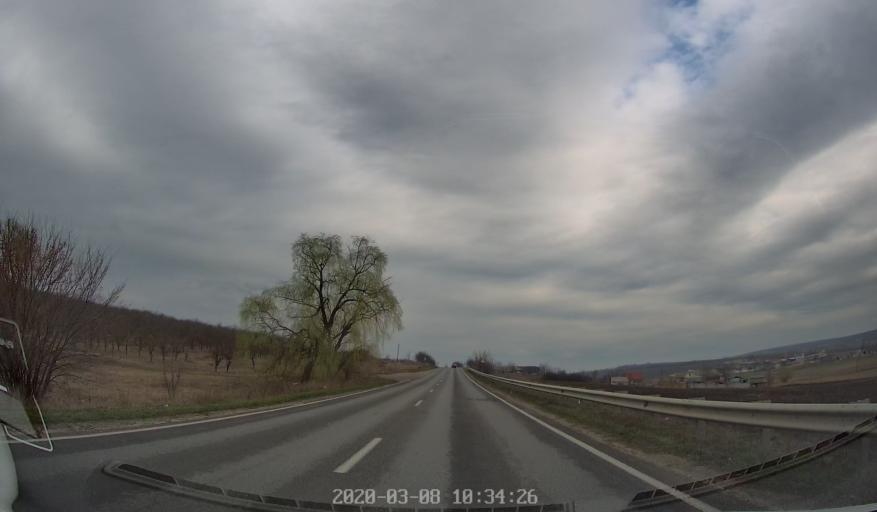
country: MD
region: Orhei
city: Orhei
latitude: 47.4119
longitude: 28.8124
